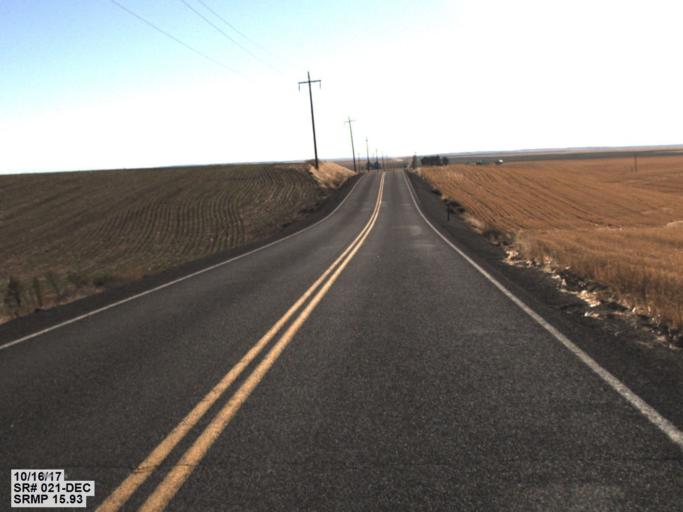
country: US
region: Washington
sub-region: Adams County
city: Ritzville
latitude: 46.8569
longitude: -118.5467
